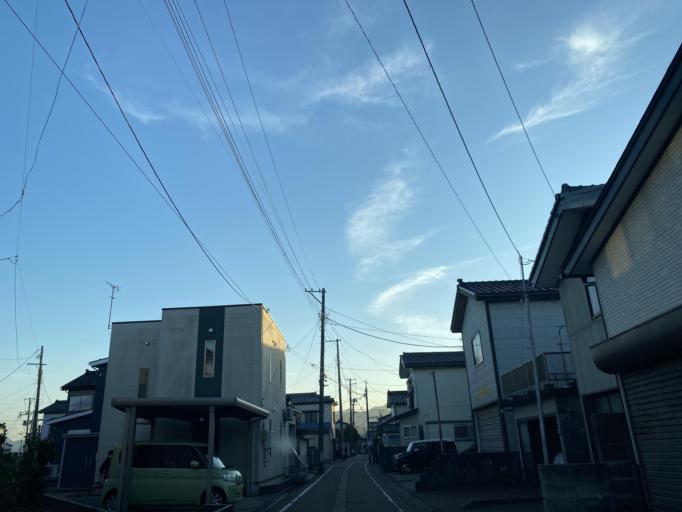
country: JP
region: Niigata
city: Kashiwazaki
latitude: 37.3736
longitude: 138.5631
